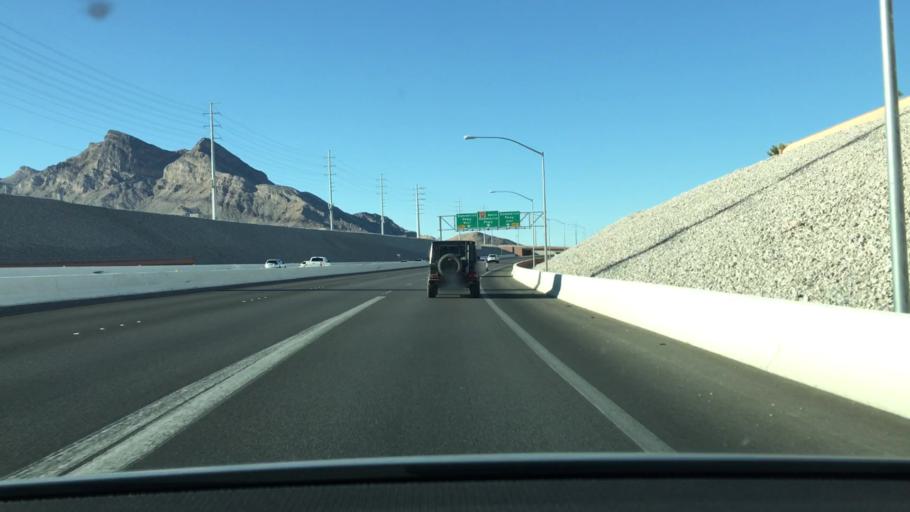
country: US
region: Nevada
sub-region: Clark County
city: Summerlin South
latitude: 36.1853
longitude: -115.3423
